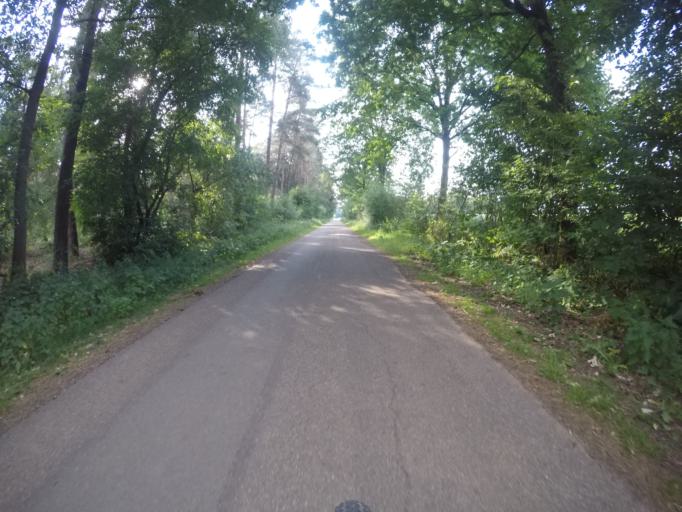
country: DE
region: North Rhine-Westphalia
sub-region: Regierungsbezirk Munster
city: Isselburg
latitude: 51.8374
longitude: 6.5098
